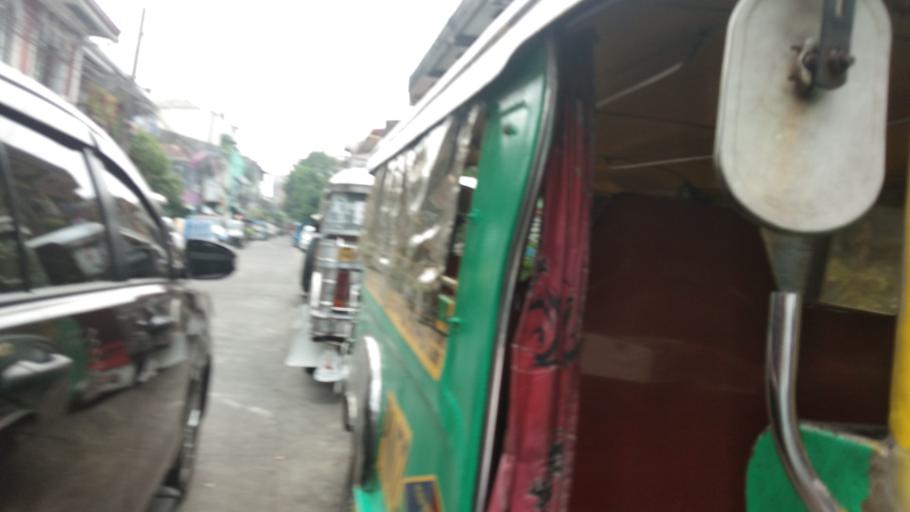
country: PH
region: Metro Manila
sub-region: City of Manila
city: Quiapo
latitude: 14.5782
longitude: 121.0008
